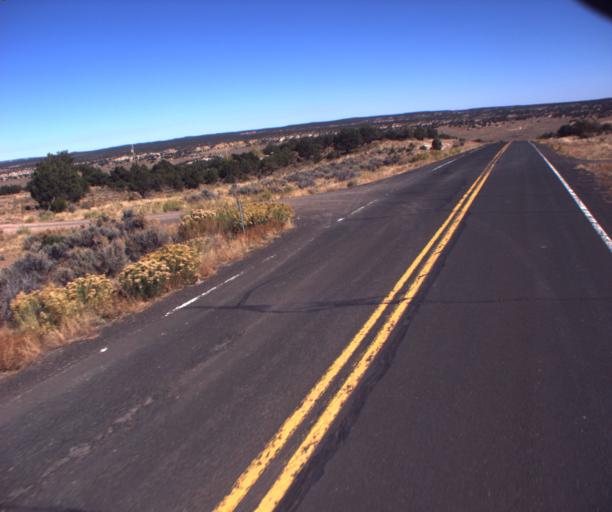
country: US
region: Arizona
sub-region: Navajo County
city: First Mesa
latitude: 35.7641
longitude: -109.9969
